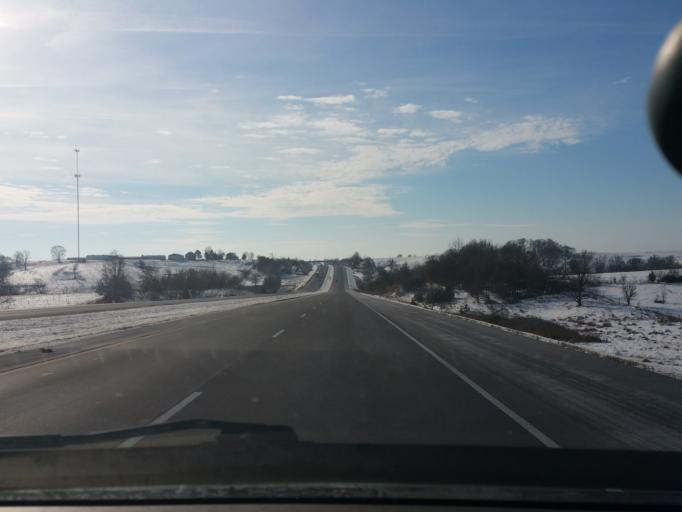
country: US
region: Iowa
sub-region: Warren County
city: Norwalk
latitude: 41.4427
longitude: -93.7802
